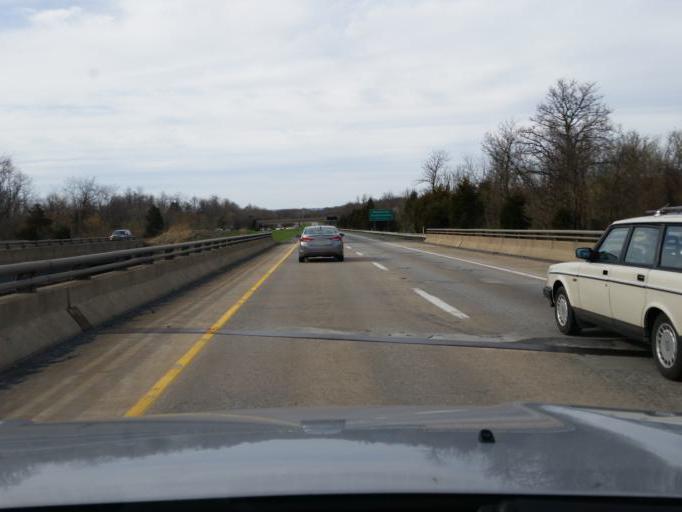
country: US
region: Pennsylvania
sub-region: Dauphin County
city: Middletown
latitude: 40.2093
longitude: -76.7066
